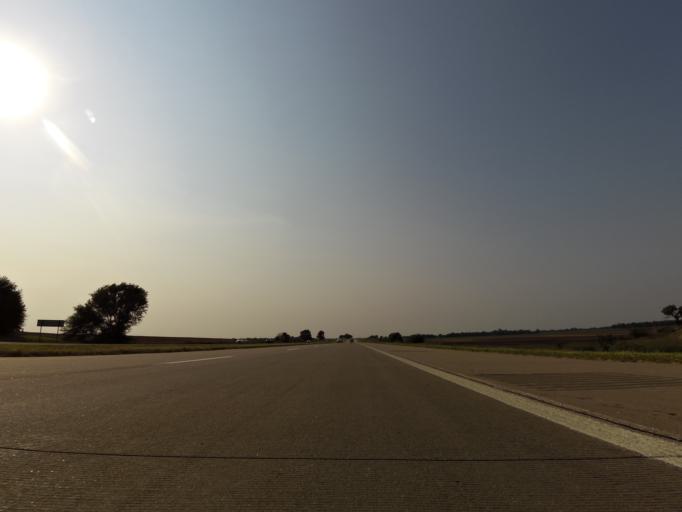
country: US
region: Kansas
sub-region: Sedgwick County
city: Colwich
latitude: 37.8559
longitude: -97.6104
